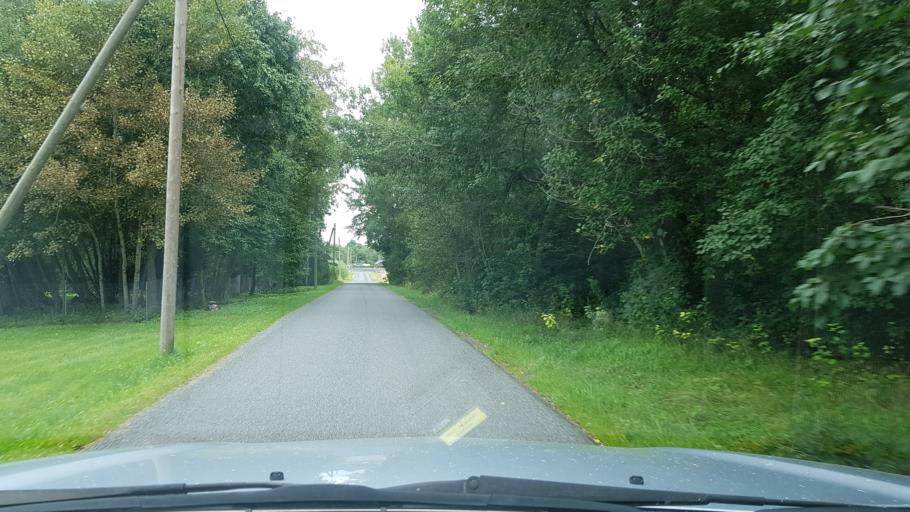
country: EE
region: Harju
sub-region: Joelaehtme vald
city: Loo
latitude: 59.3881
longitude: 24.9562
